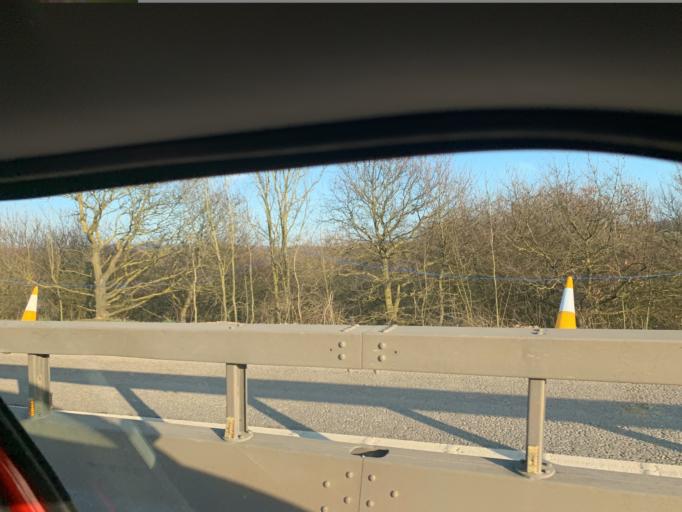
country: GB
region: England
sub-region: Surrey
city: Bletchingley
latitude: 51.2263
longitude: -0.1163
